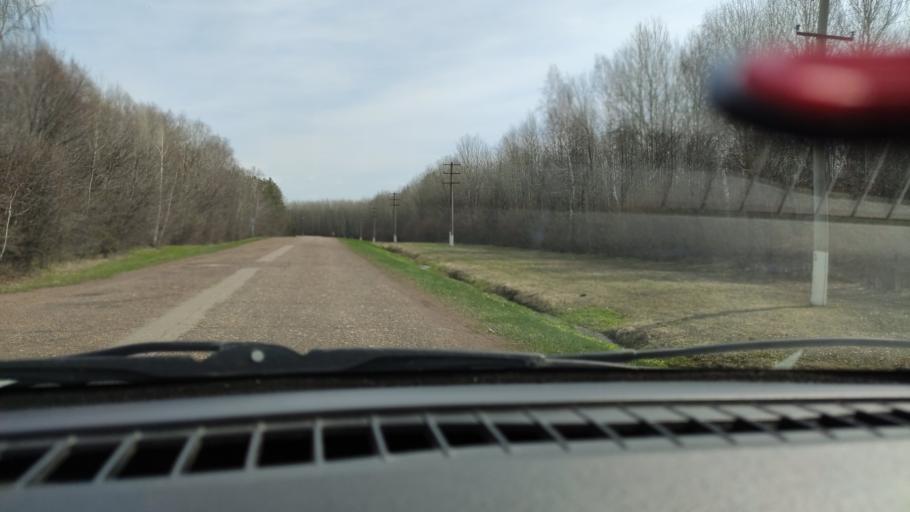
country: RU
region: Bashkortostan
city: Dyurtyuli
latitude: 55.2836
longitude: 55.0656
